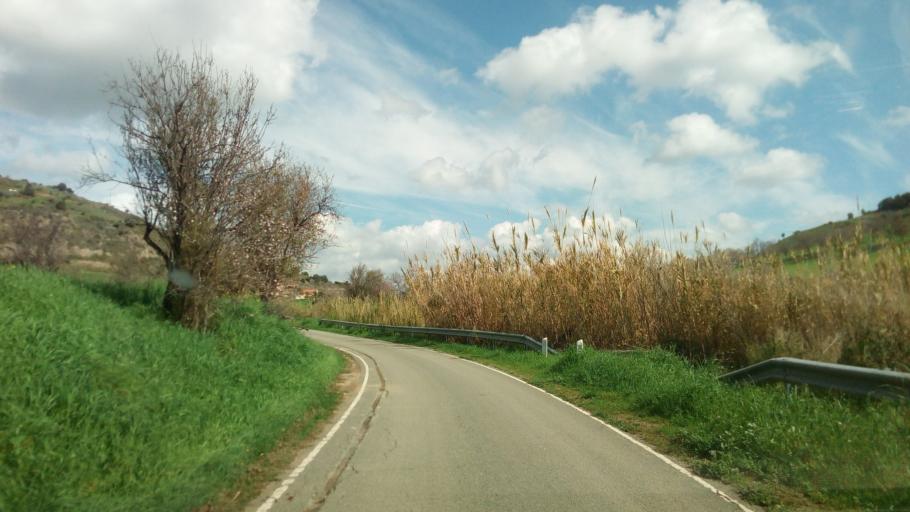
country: CY
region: Pafos
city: Mesogi
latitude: 34.7680
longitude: 32.5564
